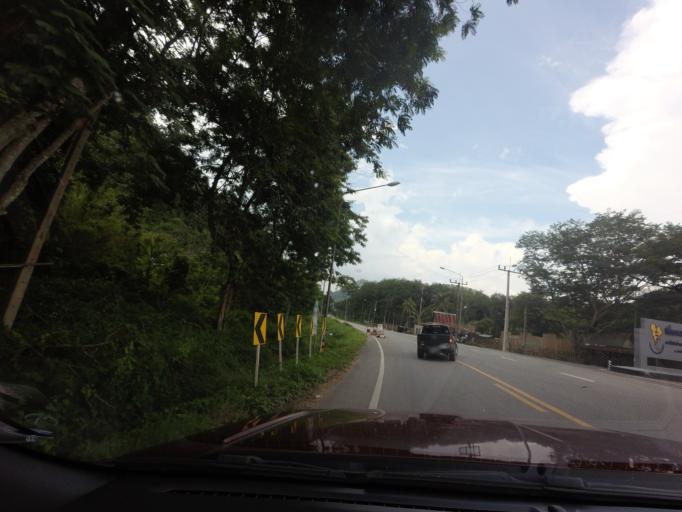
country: TH
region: Yala
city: Ban Nang Sata
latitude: 6.2339
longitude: 101.2141
